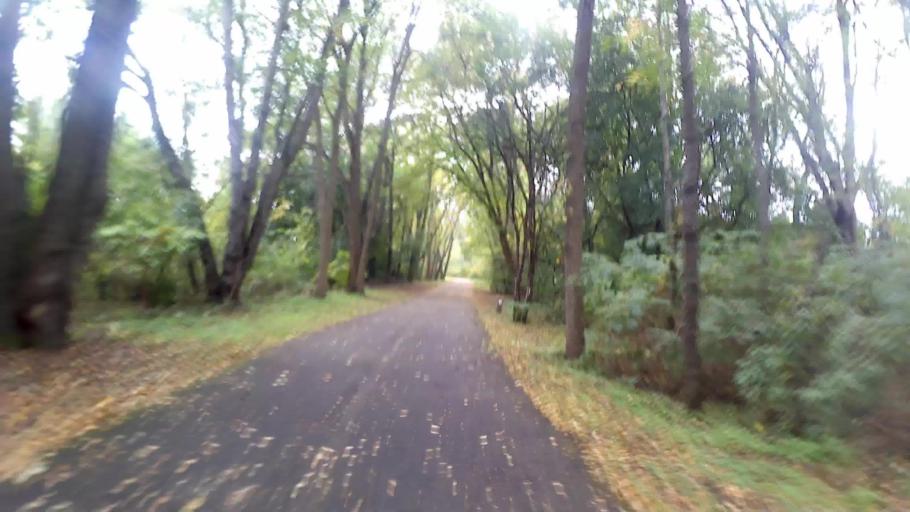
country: US
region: Illinois
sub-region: Kane County
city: Montgomery
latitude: 41.7497
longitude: -88.3709
